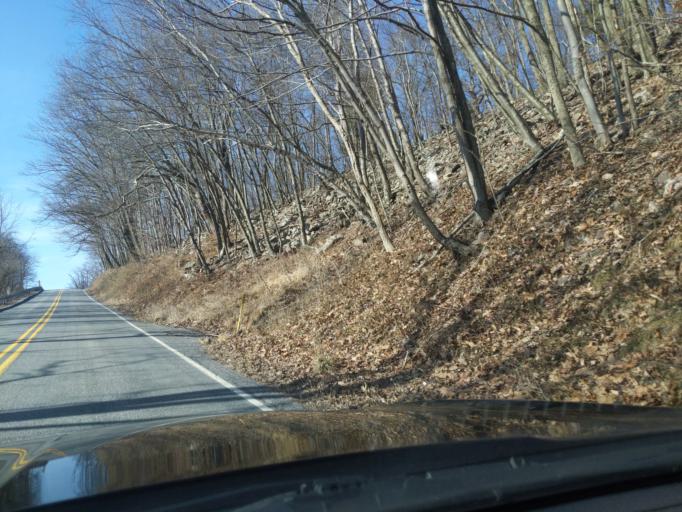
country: US
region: Pennsylvania
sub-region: Blair County
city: Tipton
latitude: 40.6213
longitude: -78.2797
